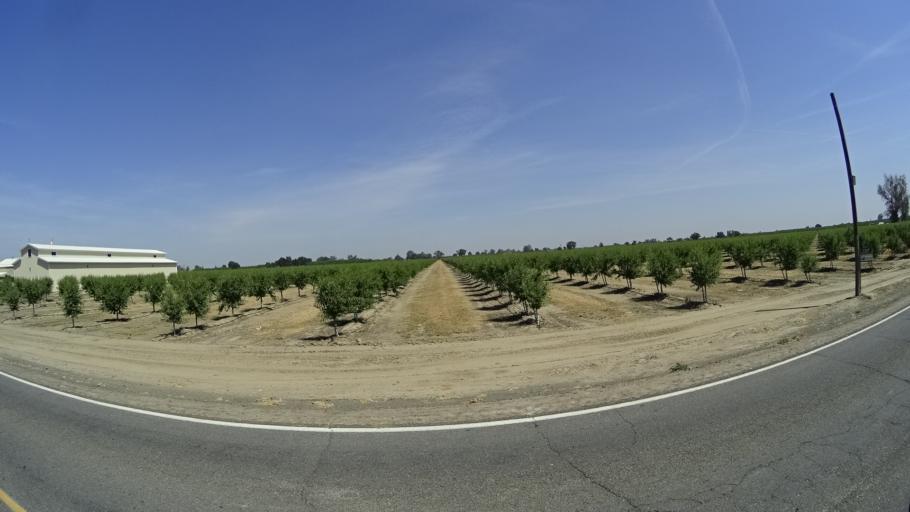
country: US
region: California
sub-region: Fresno County
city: Riverdale
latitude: 36.4019
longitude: -119.7902
